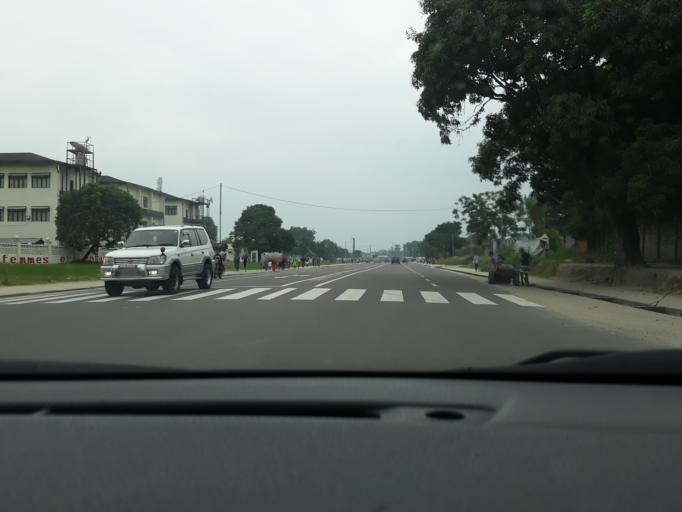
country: CD
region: Kinshasa
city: Kinshasa
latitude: -4.3313
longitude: 15.3004
